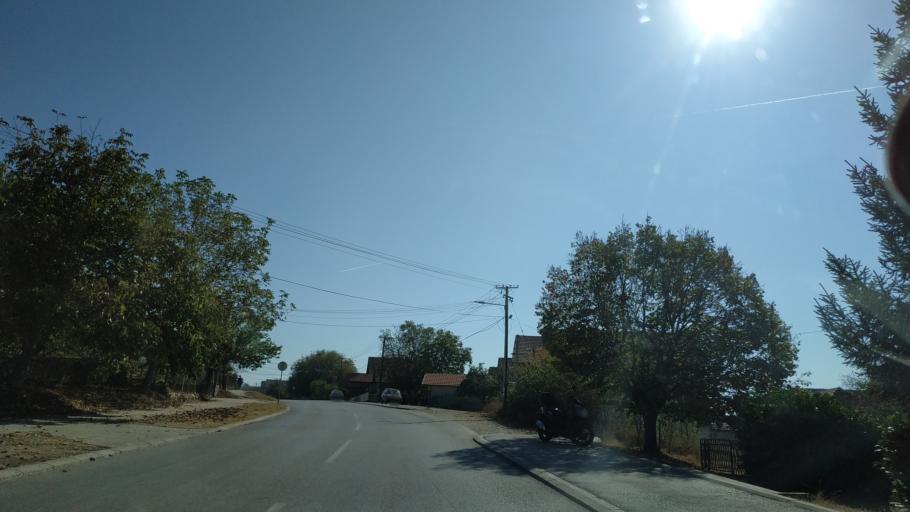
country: RS
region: Central Serbia
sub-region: Nisavski Okrug
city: Aleksinac
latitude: 43.5475
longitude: 21.6933
